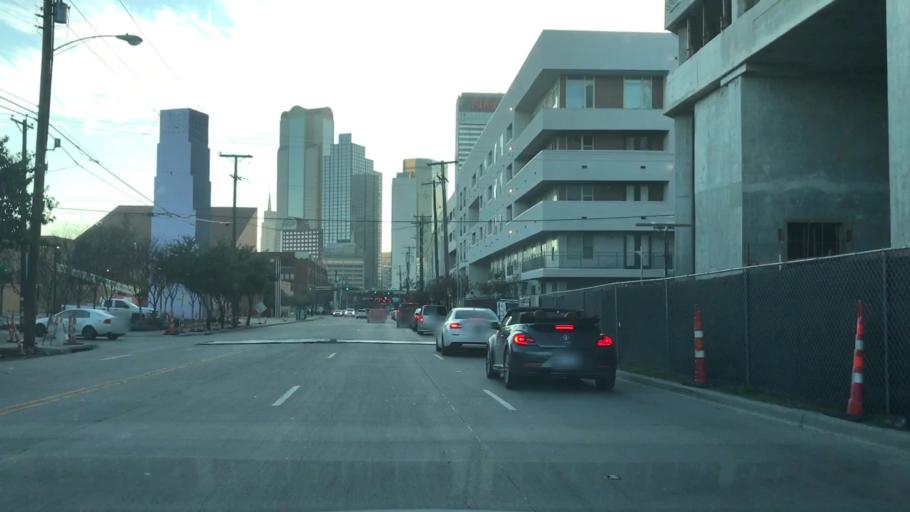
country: US
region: Texas
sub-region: Dallas County
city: Dallas
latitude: 32.7889
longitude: -96.7891
